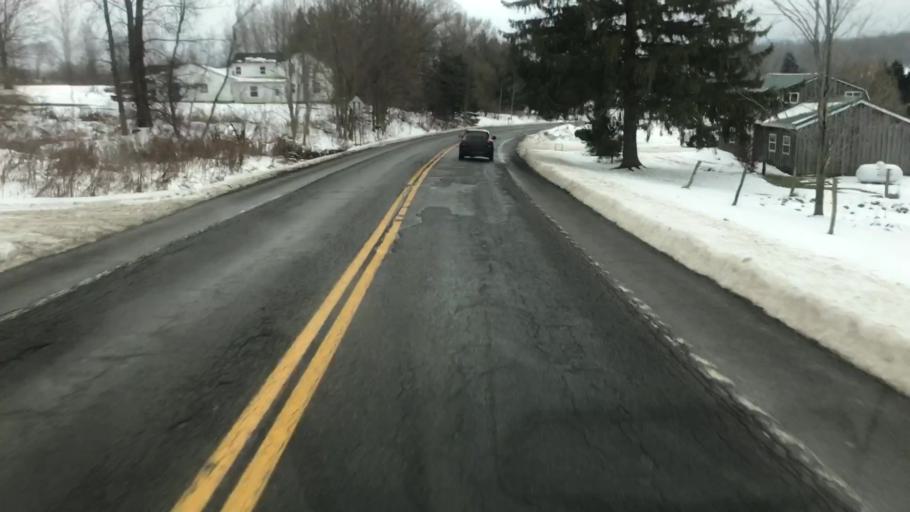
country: US
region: New York
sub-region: Cayuga County
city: Moravia
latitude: 42.7327
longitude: -76.3139
